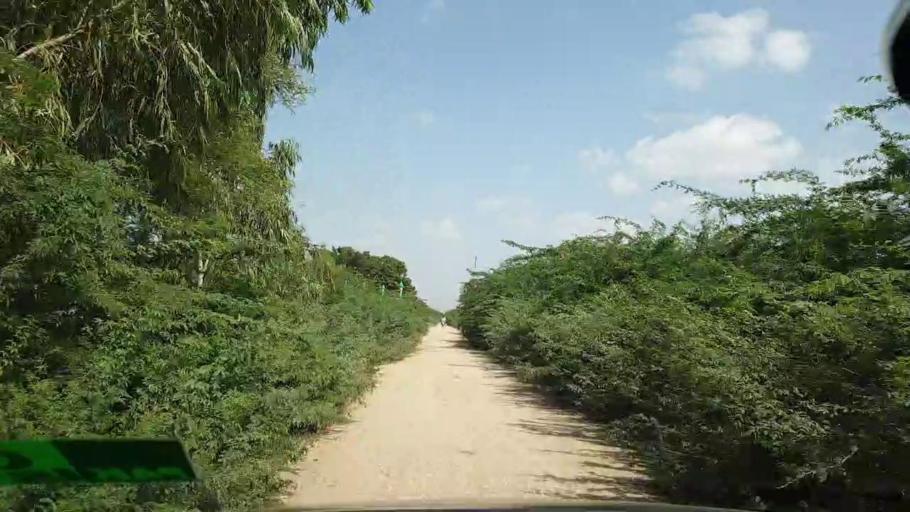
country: PK
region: Sindh
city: Naukot
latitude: 24.6448
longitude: 69.2314
